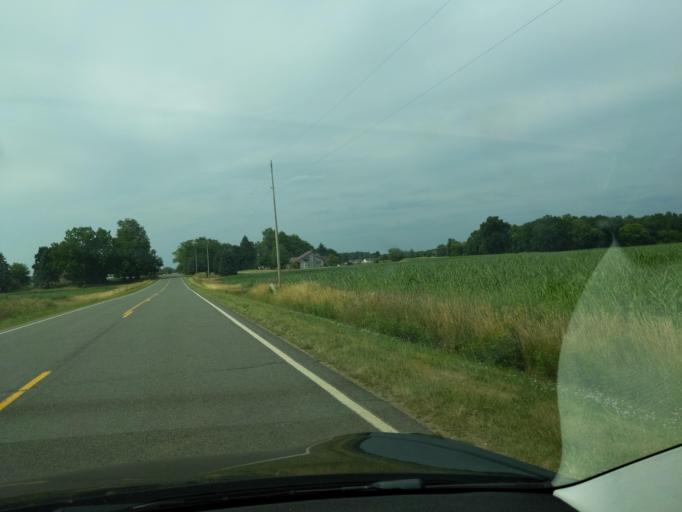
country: US
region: Michigan
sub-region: Clinton County
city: DeWitt
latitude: 42.9230
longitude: -84.6020
